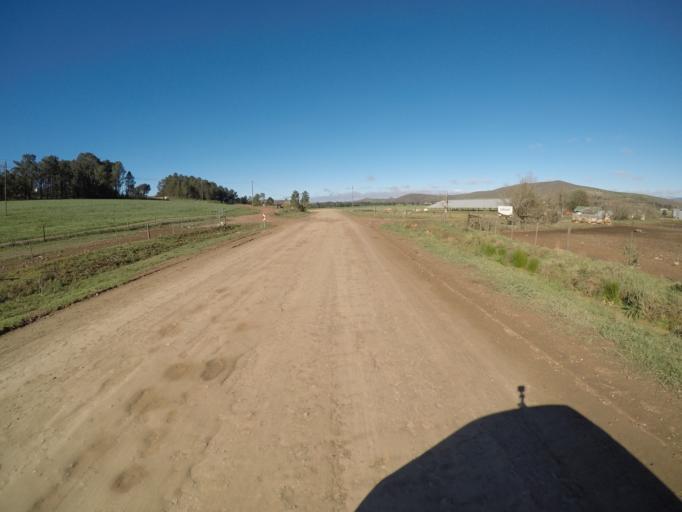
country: ZA
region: Western Cape
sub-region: Overberg District Municipality
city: Caledon
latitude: -34.0686
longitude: 19.6311
